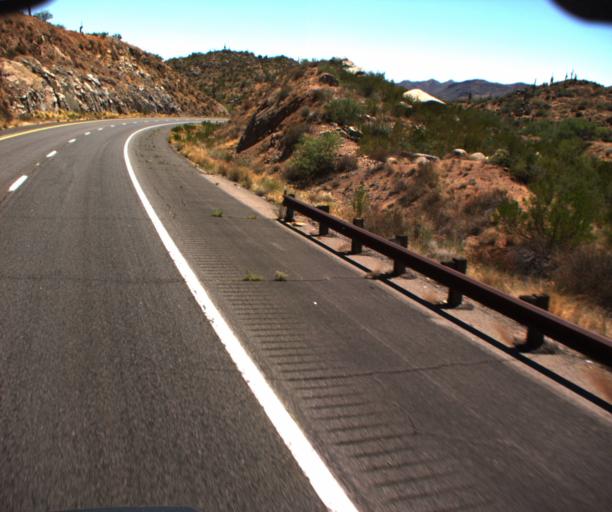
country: US
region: Arizona
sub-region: Gila County
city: Tonto Basin
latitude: 33.8194
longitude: -111.4774
